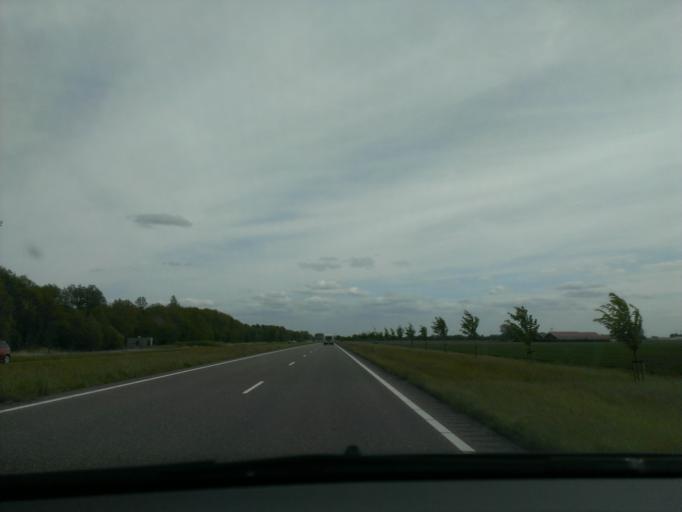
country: NL
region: Flevoland
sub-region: Gemeente Lelystad
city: Lelystad
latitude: 52.4502
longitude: 5.5454
